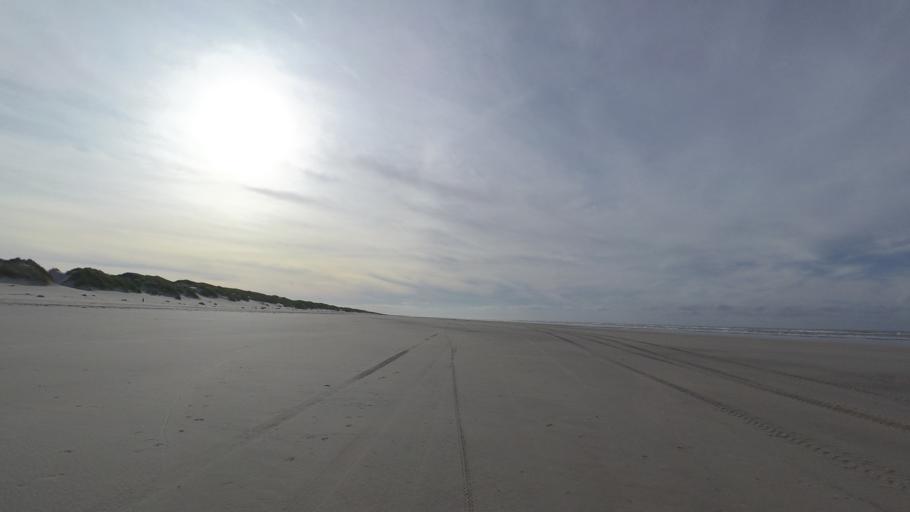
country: NL
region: Friesland
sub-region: Gemeente Dongeradeel
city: Holwerd
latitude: 53.4661
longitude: 5.8778
